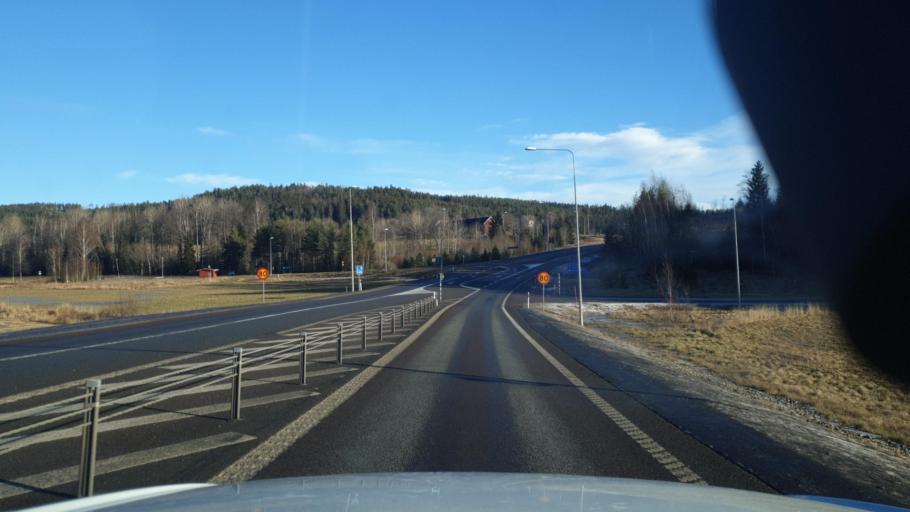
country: SE
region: Vaermland
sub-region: Arvika Kommun
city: Arvika
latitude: 59.6673
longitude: 12.7947
